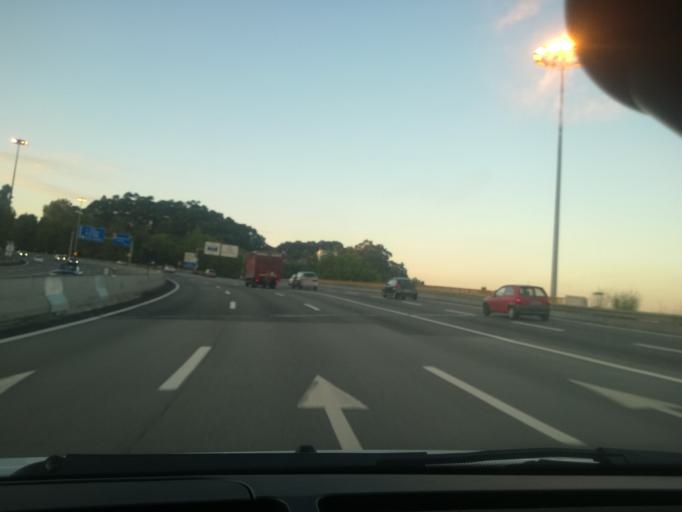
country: PT
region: Porto
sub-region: Gondomar
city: Valbom
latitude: 41.1496
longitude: -8.5788
